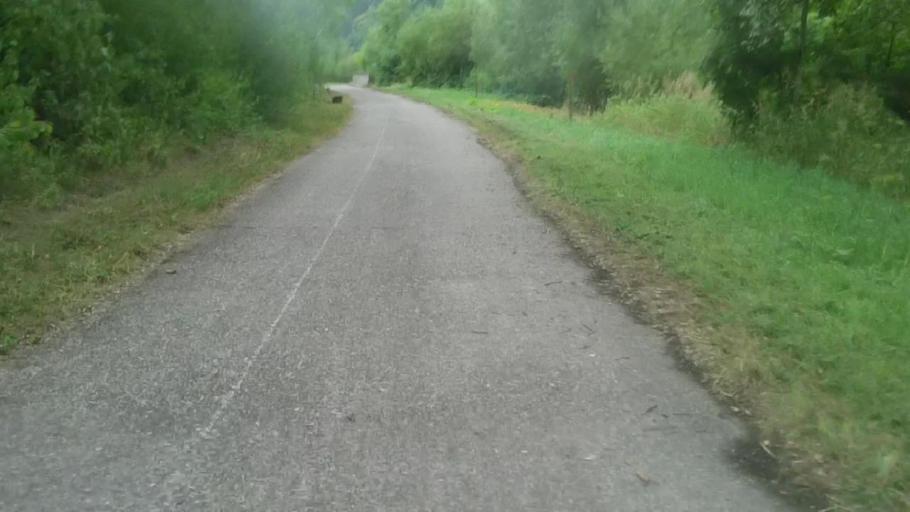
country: DE
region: Rheinland-Pfalz
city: Serrig
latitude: 49.5795
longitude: 6.5652
